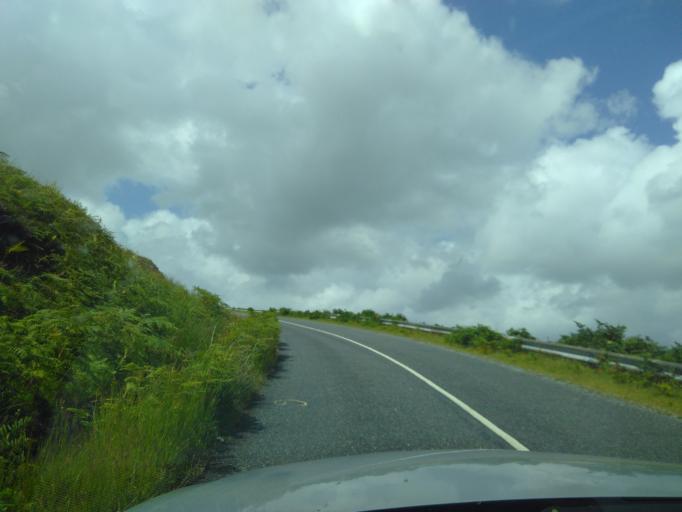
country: IE
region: Ulster
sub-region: County Donegal
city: Buncrana
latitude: 55.1864
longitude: -7.5888
